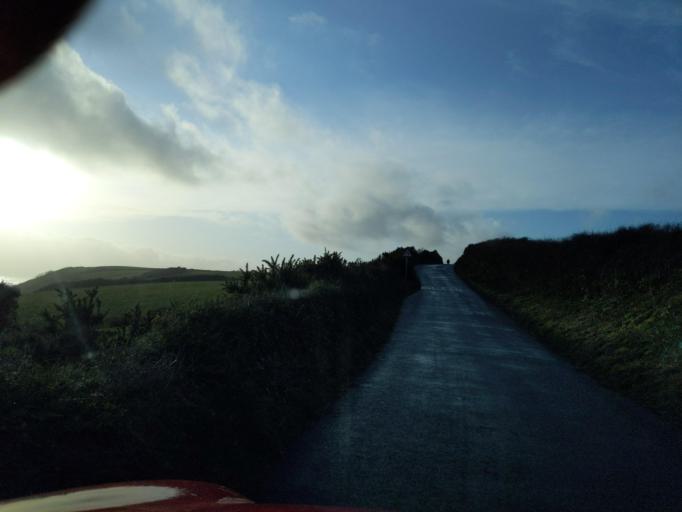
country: GB
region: England
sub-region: Cornwall
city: Fowey
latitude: 50.3312
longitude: -4.6097
